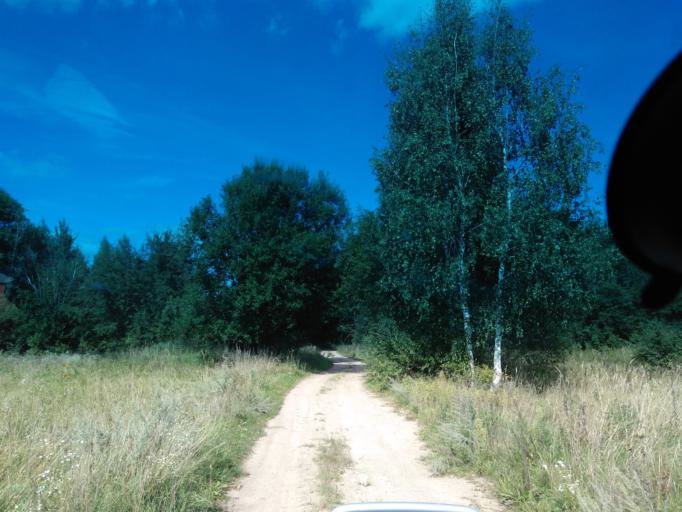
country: BY
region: Minsk
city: Stan'kava
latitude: 53.6267
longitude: 27.3143
